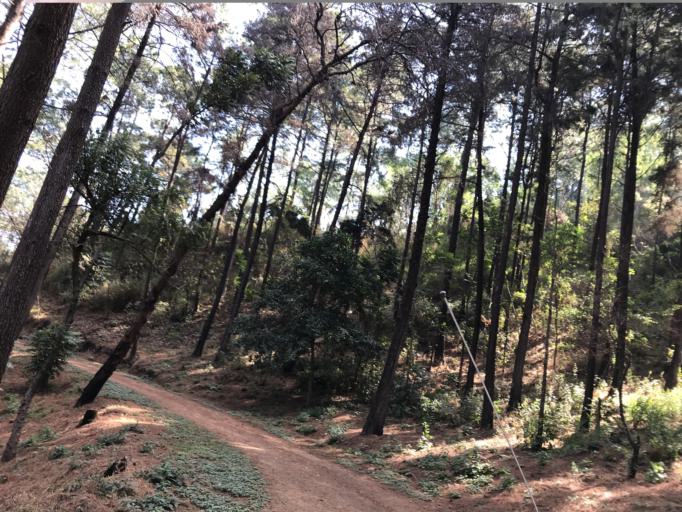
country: GT
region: Guatemala
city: Petapa
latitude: 14.4828
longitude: -90.5535
